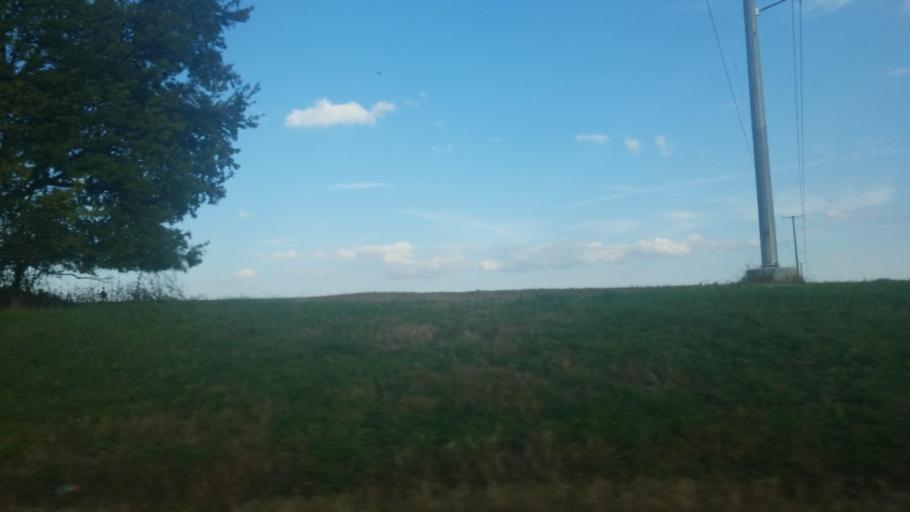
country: US
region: Illinois
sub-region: Saline County
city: Harrisburg
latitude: 37.8305
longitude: -88.6146
